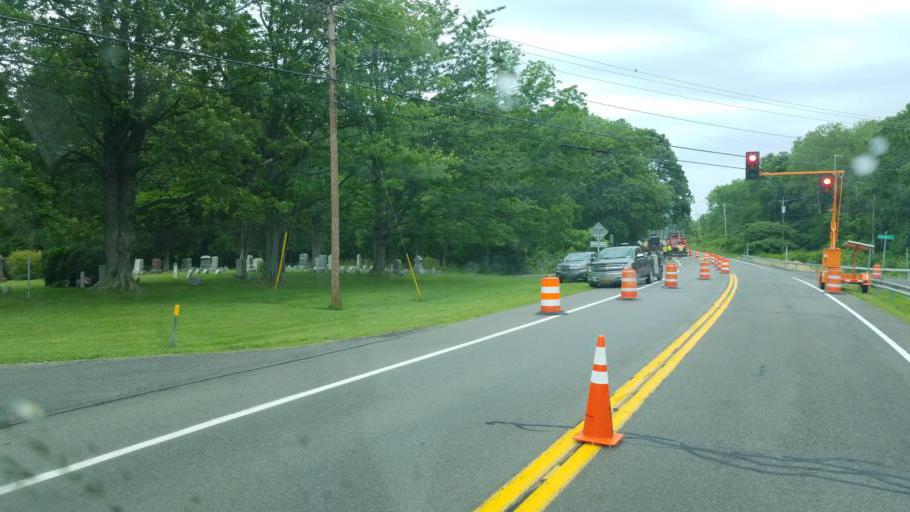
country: US
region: New York
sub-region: Niagara County
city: Youngstown
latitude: 43.2694
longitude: -78.9949
